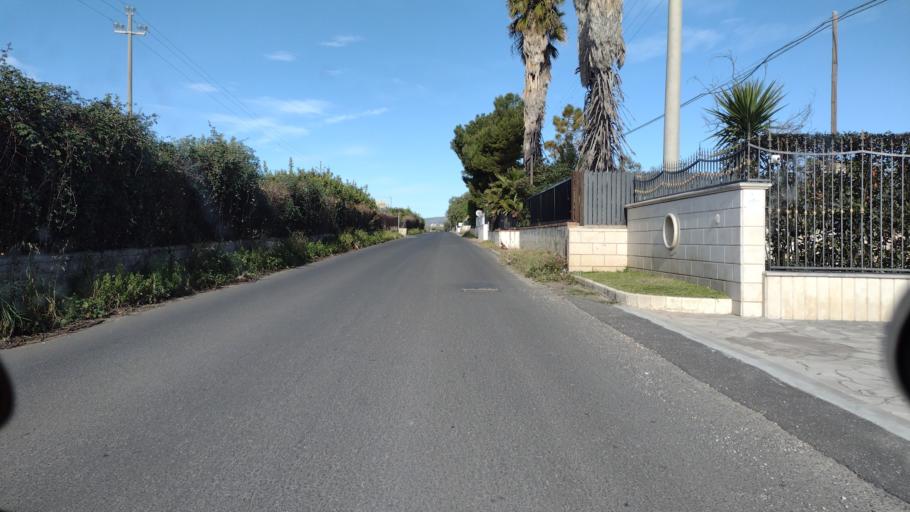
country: IT
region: Sicily
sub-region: Provincia di Siracusa
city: Avola
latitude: 36.8754
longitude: 15.1111
